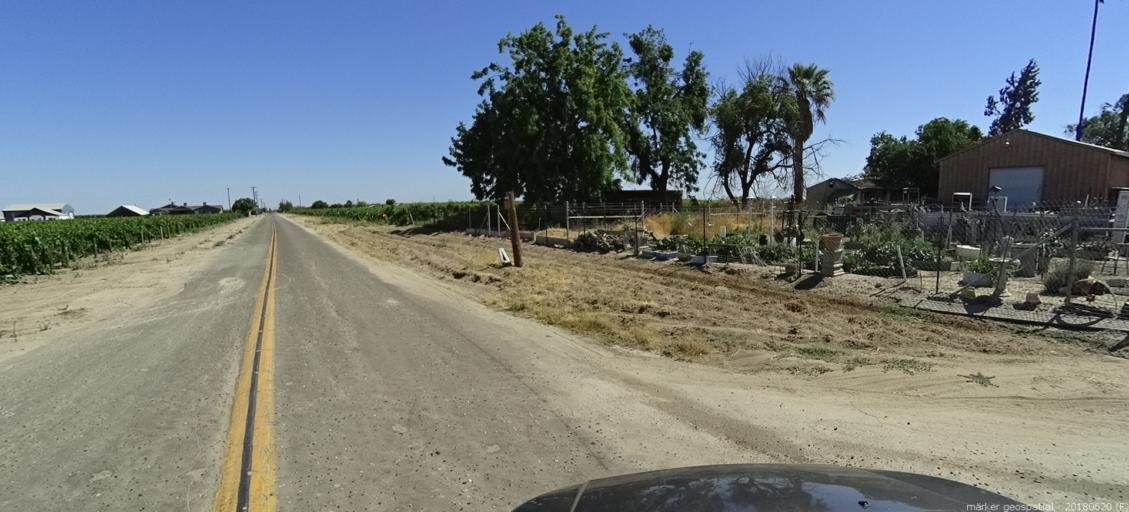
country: US
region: California
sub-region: Fresno County
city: Biola
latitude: 36.8369
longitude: -120.0100
